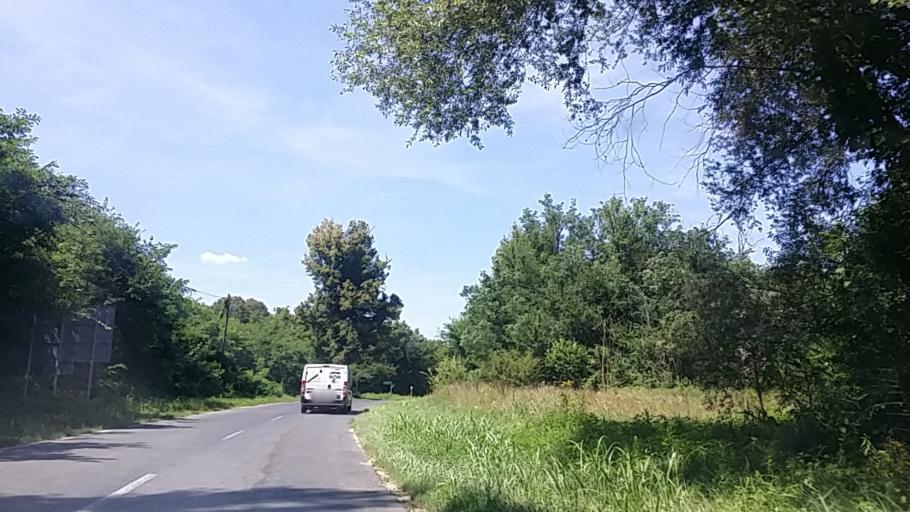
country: HU
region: Somogy
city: Karad
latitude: 46.7272
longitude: 17.7731
